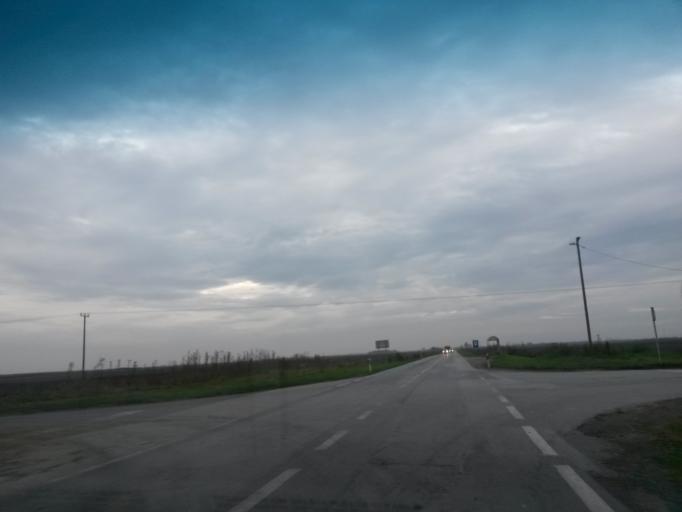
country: HR
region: Vukovarsko-Srijemska
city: Bobota
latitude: 45.4432
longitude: 18.8745
